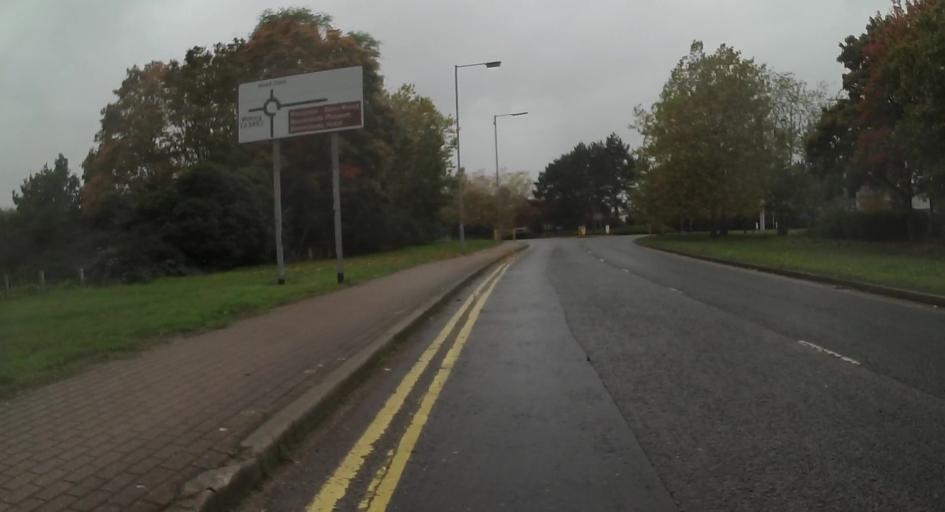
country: GB
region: England
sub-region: Surrey
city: Byfleet
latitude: 51.3474
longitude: -0.4711
